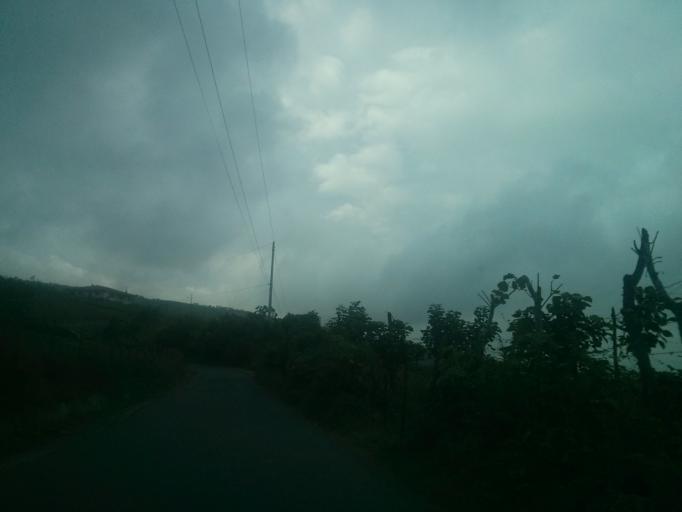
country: CR
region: Cartago
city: Cot
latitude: 9.9002
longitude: -83.7978
